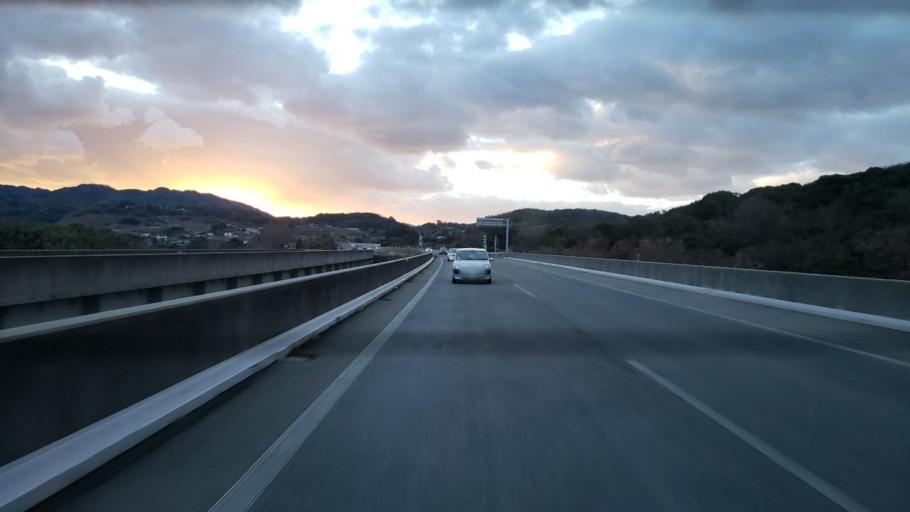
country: JP
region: Hyogo
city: Akashi
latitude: 34.5329
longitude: 134.9615
